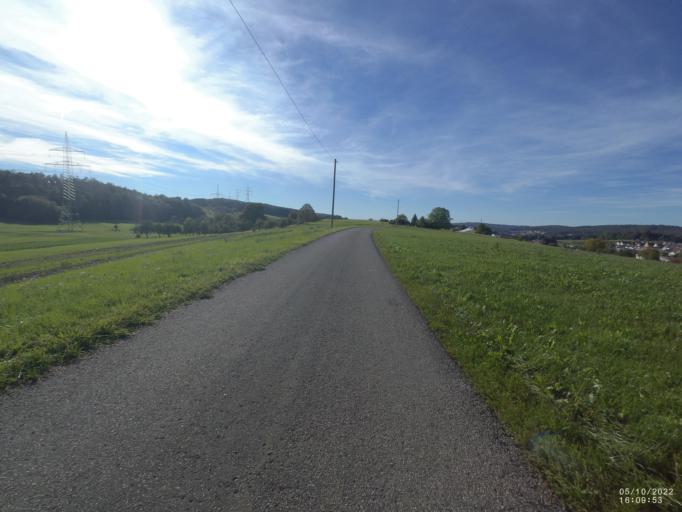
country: DE
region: Baden-Wuerttemberg
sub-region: Regierungsbezirk Stuttgart
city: Ebersbach an der Fils
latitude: 48.7014
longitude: 9.5109
